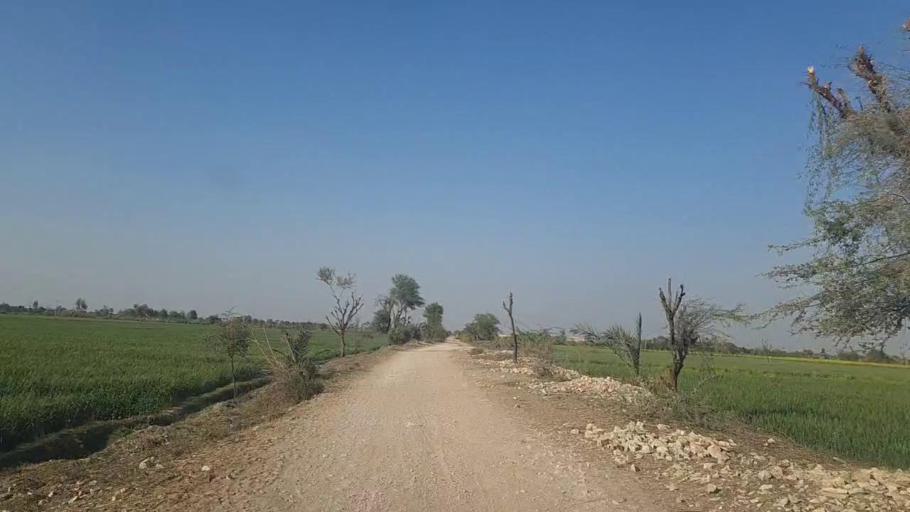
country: PK
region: Sindh
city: Jam Sahib
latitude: 26.3150
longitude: 68.7149
